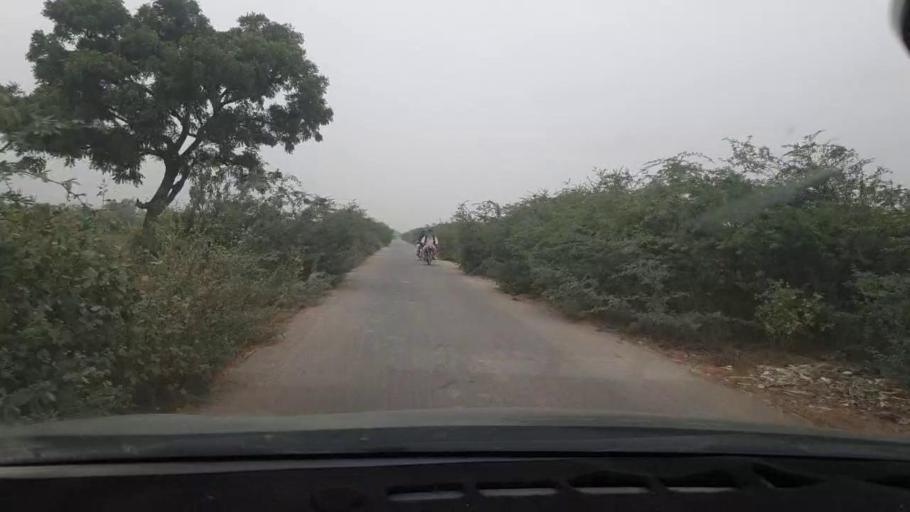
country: PK
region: Sindh
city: Malir Cantonment
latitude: 24.9252
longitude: 67.3283
